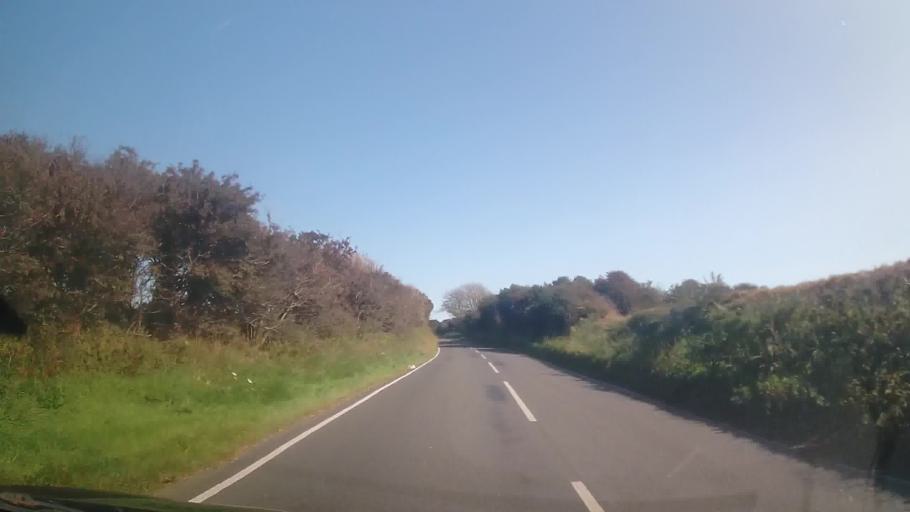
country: GB
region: Wales
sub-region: Pembrokeshire
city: Mathry
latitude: 51.9433
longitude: -5.0595
